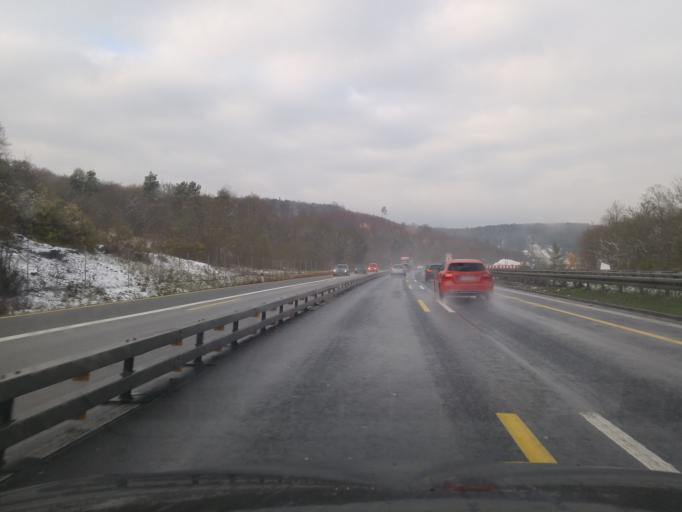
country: DE
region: Bavaria
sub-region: Regierungsbezirk Unterfranken
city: Fuchsstadt
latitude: 50.1048
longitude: 9.9664
